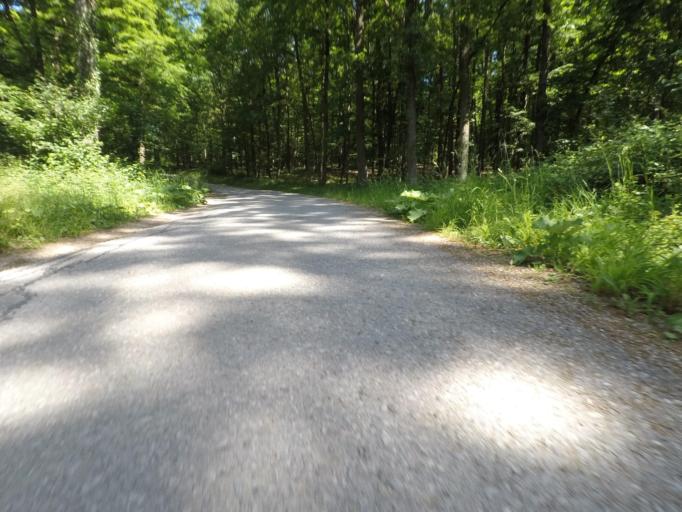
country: AT
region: Lower Austria
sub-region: Politischer Bezirk Modling
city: Perchtoldsdorf
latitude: 48.1731
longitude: 16.2436
